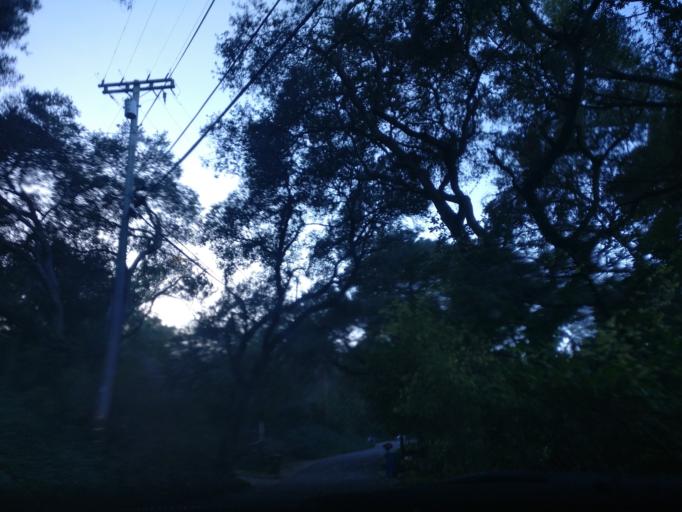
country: US
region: California
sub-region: Contra Costa County
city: Orinda
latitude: 37.8854
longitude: -122.1997
